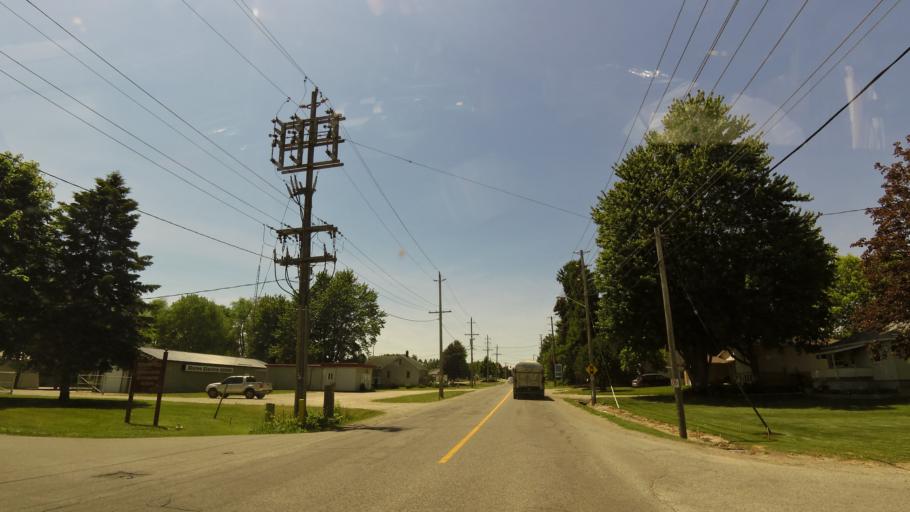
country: CA
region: Ontario
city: Ingersoll
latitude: 42.8787
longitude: -80.7437
